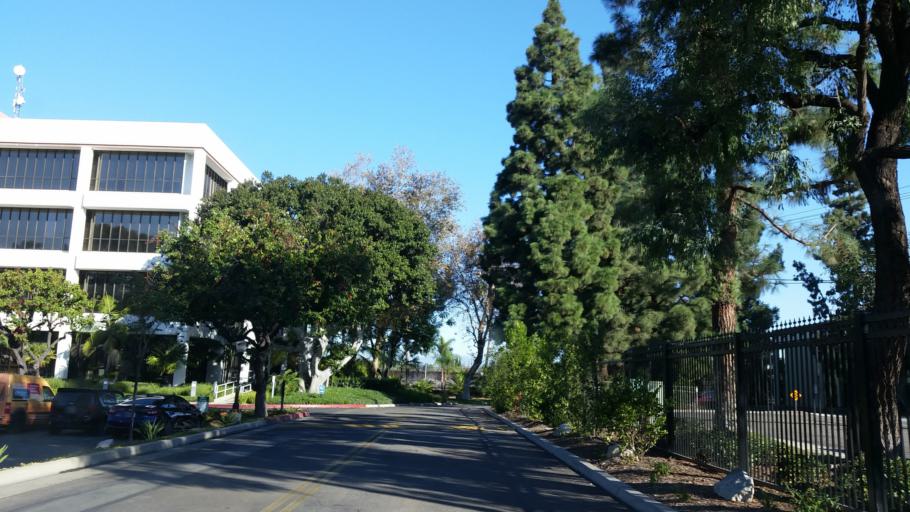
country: US
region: California
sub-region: Orange County
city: Buena Park
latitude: 33.8484
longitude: -117.9680
